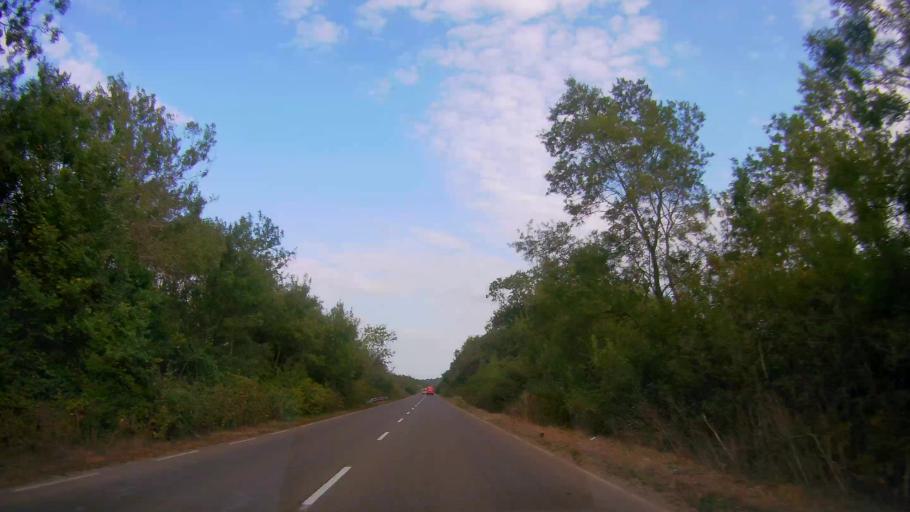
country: BG
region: Burgas
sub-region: Obshtina Sozopol
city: Sozopol
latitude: 42.3522
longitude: 27.7092
